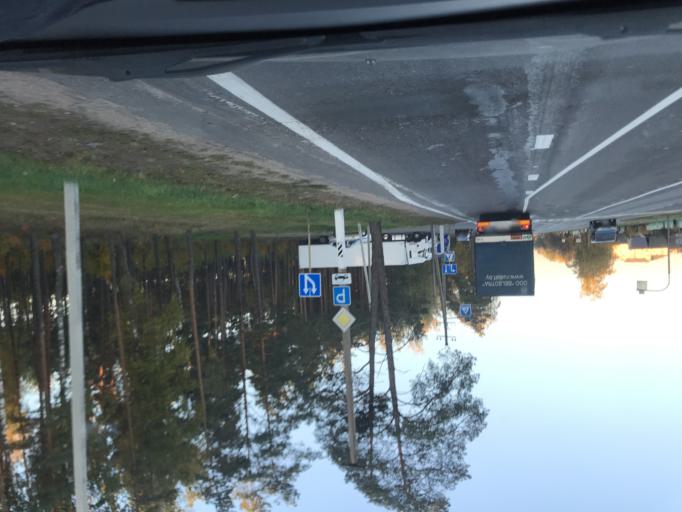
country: BY
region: Minsk
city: Staryya Darohi
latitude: 53.0332
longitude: 28.2505
